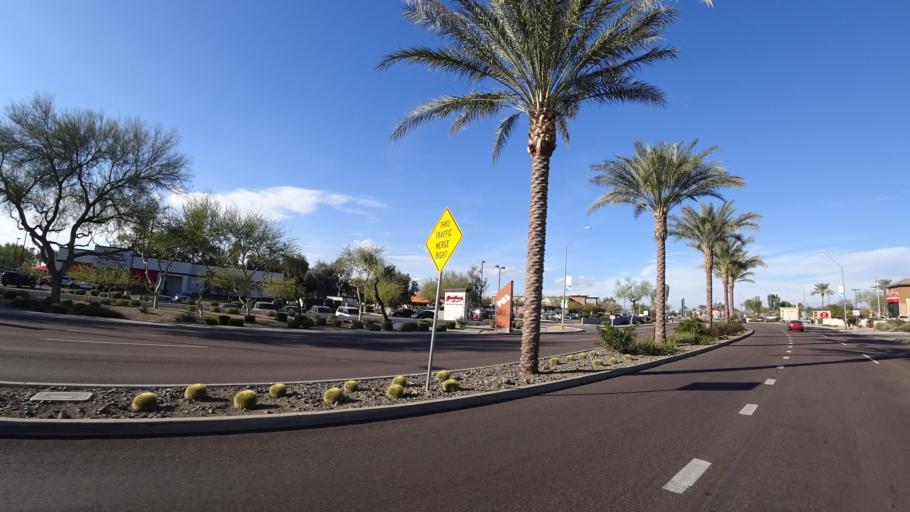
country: US
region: Arizona
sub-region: Maricopa County
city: Sun City
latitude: 33.6350
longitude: -112.2338
